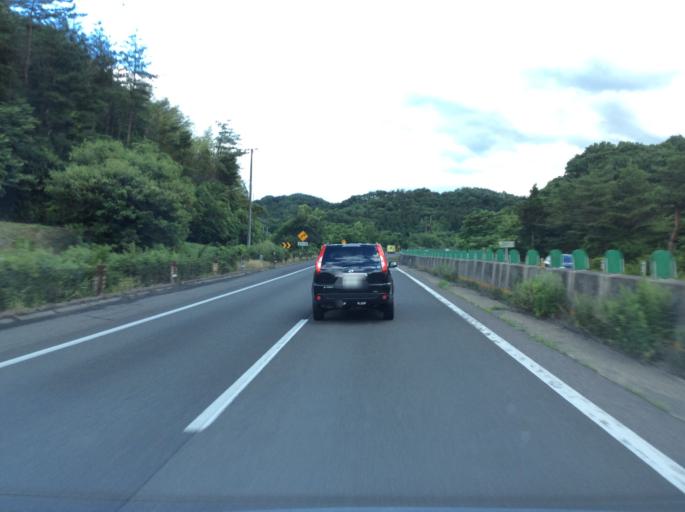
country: JP
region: Fukushima
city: Nihommatsu
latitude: 37.6349
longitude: 140.4339
